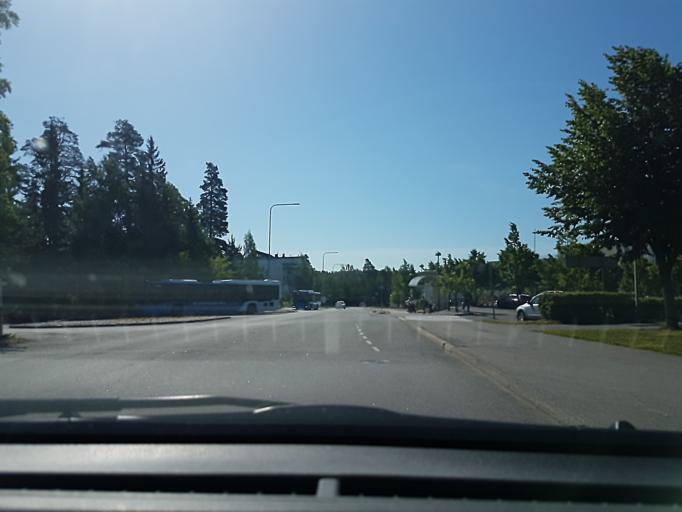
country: FI
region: Uusimaa
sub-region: Helsinki
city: Vantaa
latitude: 60.3326
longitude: 25.0598
